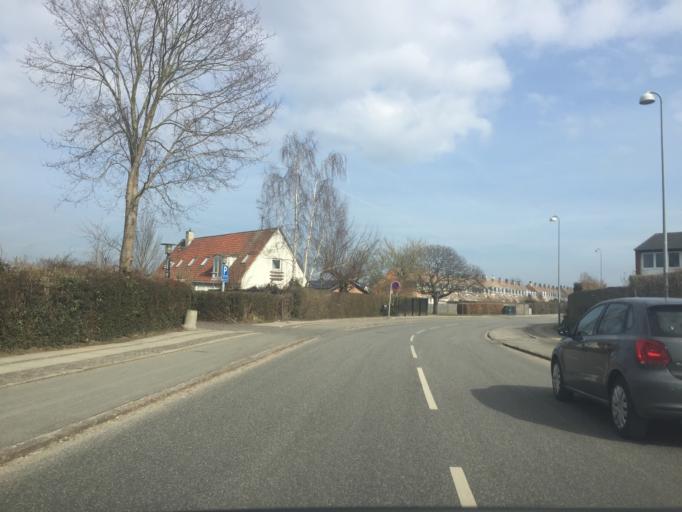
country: DK
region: Capital Region
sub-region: Rudersdal Kommune
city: Holte
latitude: 55.7902
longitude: 12.4803
